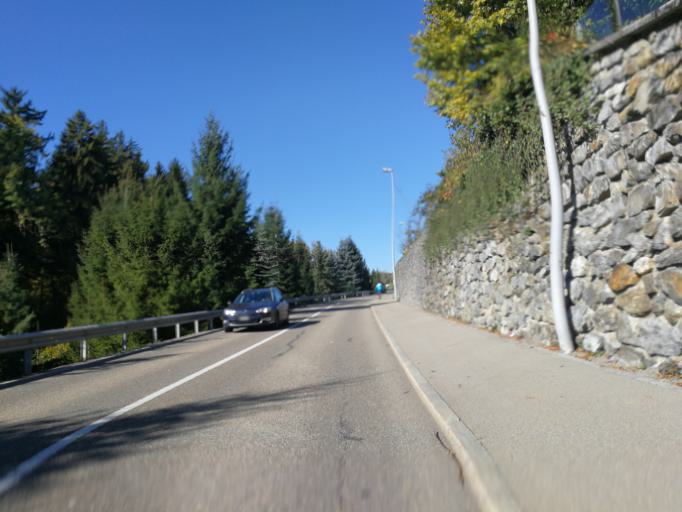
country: CH
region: Zurich
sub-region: Bezirk Meilen
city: Hombrechtikon
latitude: 47.2473
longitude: 8.7709
